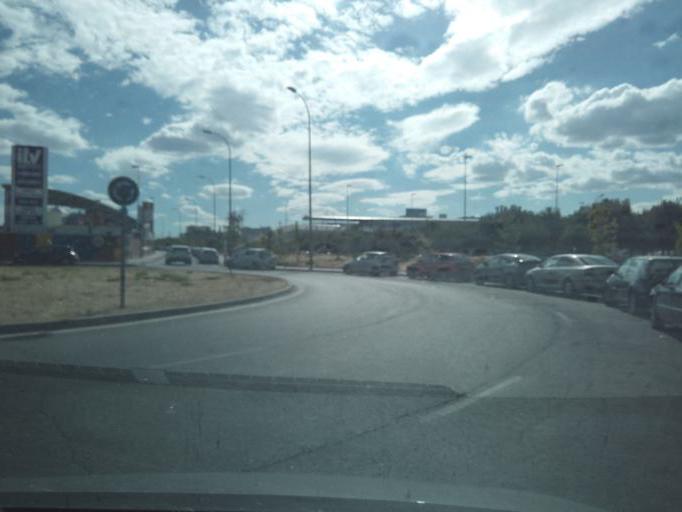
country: ES
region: Madrid
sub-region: Provincia de Madrid
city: Las Tablas
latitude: 40.4991
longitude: -3.6610
